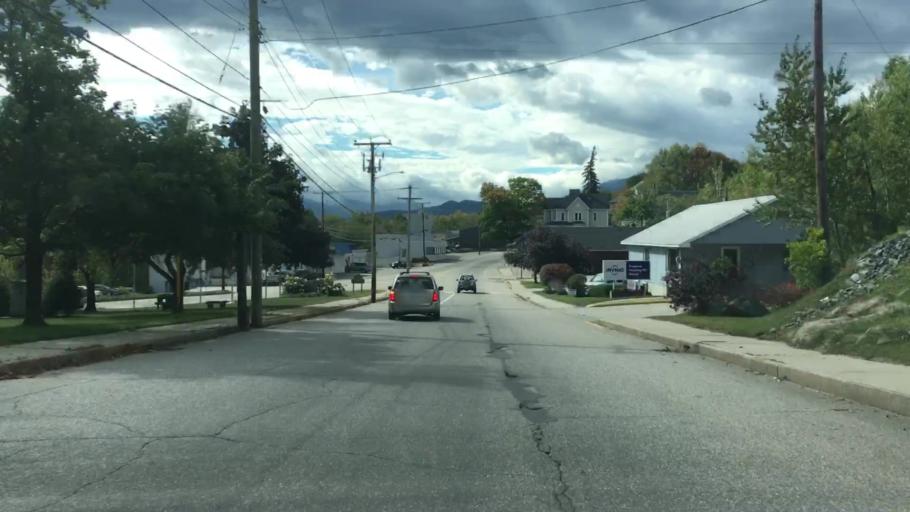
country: US
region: New Hampshire
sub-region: Coos County
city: Berlin
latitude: 44.4656
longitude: -71.1853
